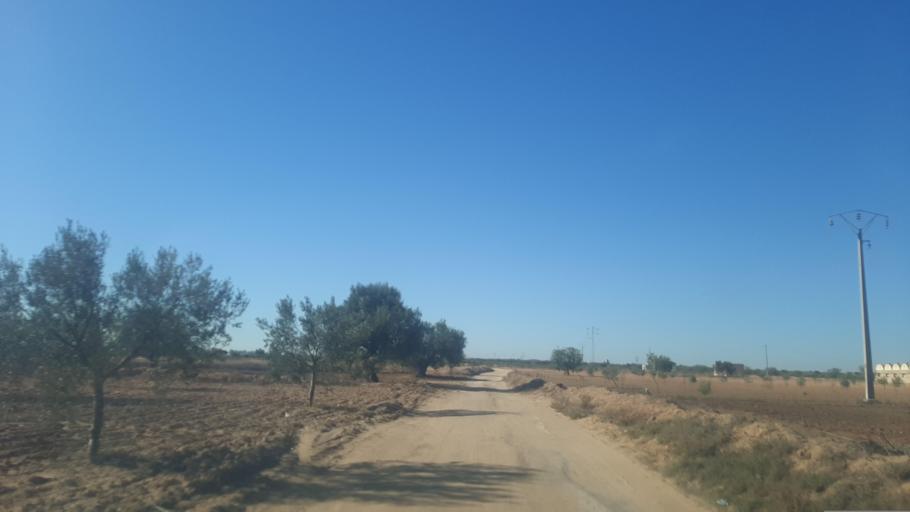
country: TN
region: Safaqis
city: Sfax
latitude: 34.8861
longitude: 10.5855
